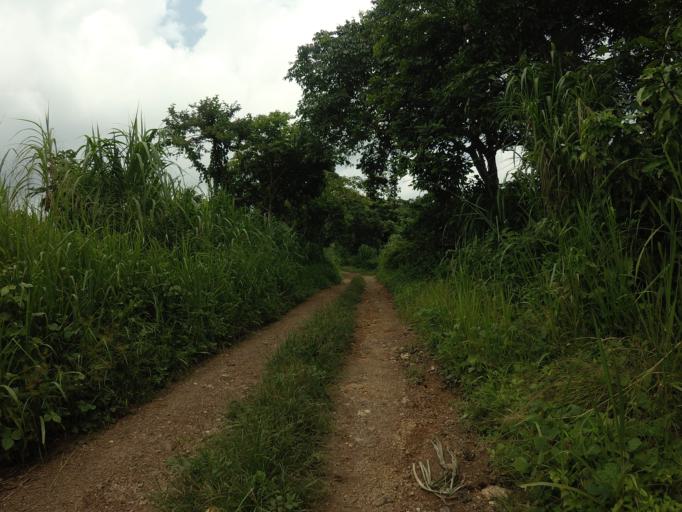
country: TG
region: Plateaux
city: Kpalime
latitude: 6.8434
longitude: 0.4447
